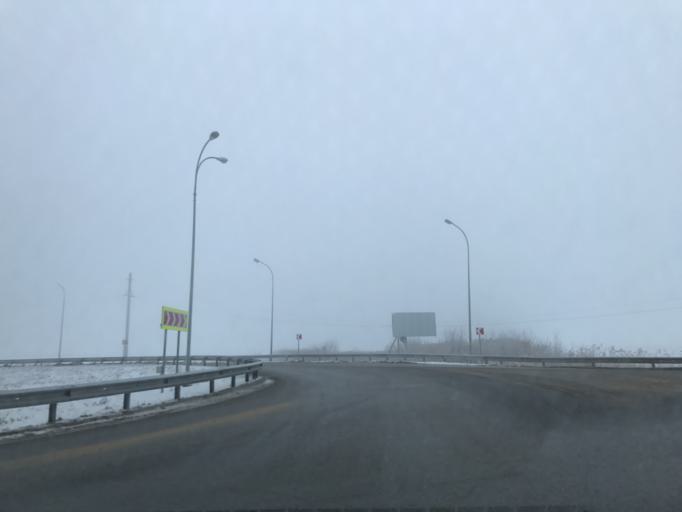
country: RU
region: Rostov
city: Temernik
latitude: 47.3705
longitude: 39.7892
